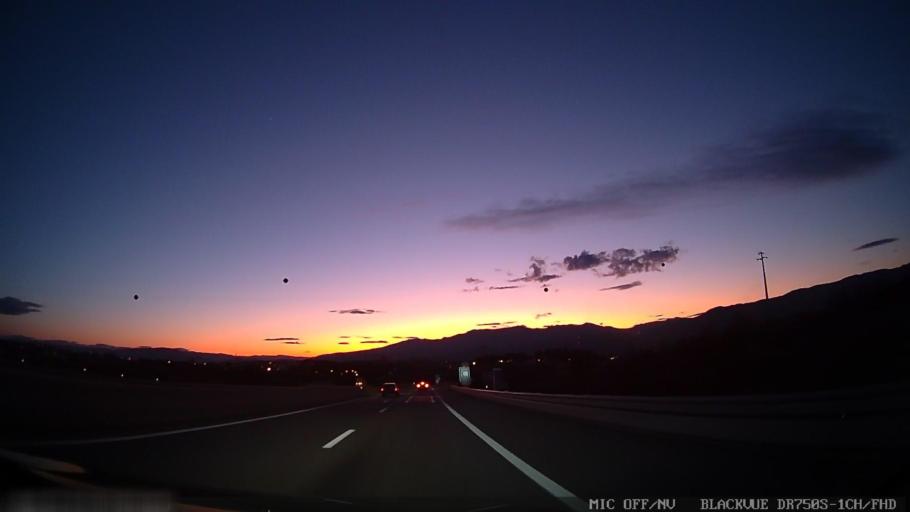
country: PT
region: Vila Real
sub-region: Vila Real
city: Vila Real
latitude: 41.2875
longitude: -7.6989
